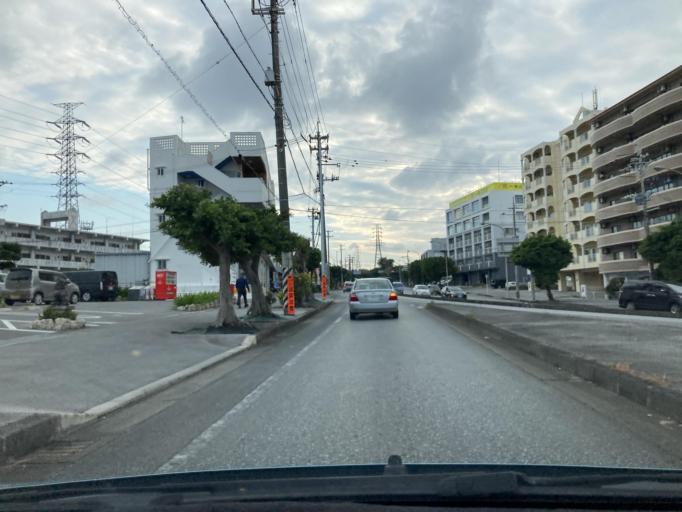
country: JP
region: Okinawa
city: Okinawa
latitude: 26.3541
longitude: 127.8052
